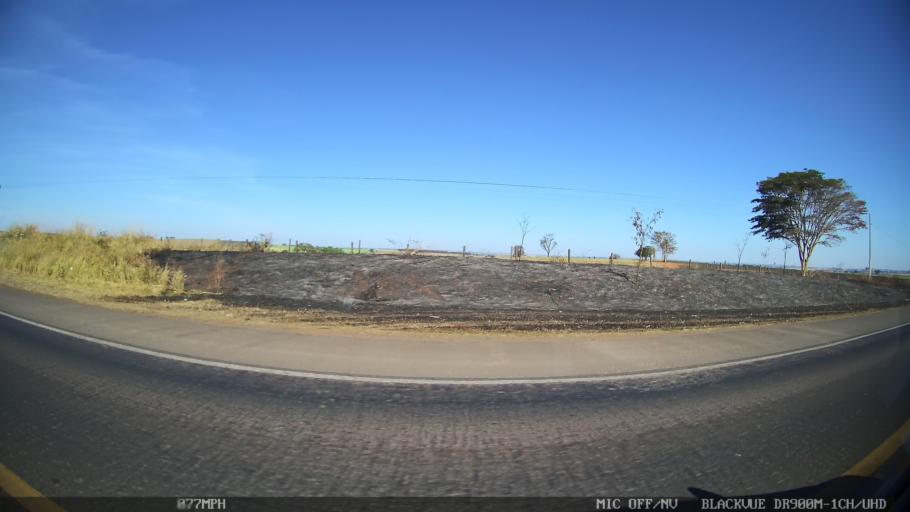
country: BR
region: Sao Paulo
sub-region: Olimpia
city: Olimpia
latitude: -20.6621
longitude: -48.8617
